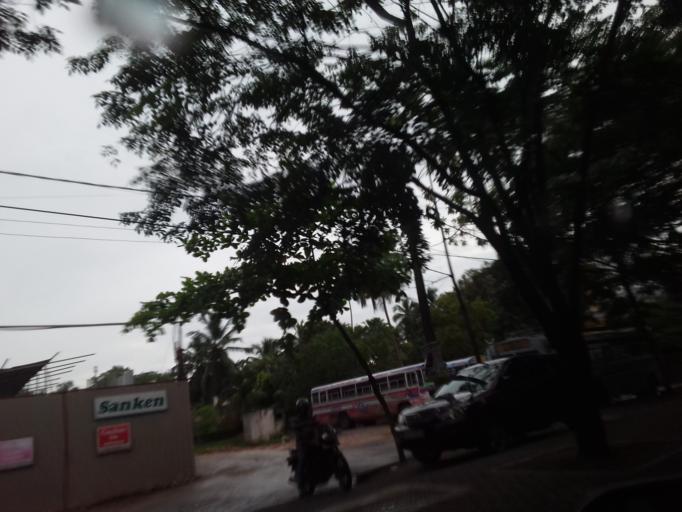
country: LK
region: Western
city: Battaramulla South
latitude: 6.9024
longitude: 79.9281
